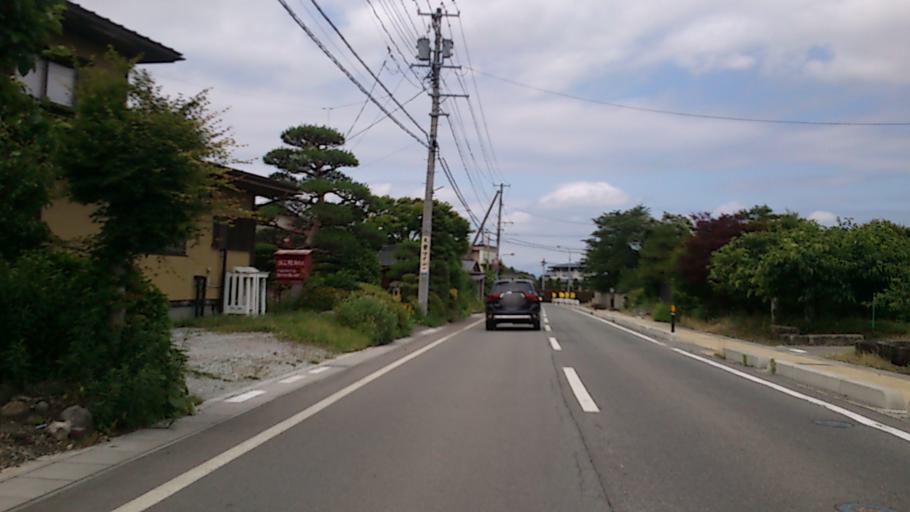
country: JP
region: Yamagata
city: Tendo
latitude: 38.3155
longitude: 140.4010
